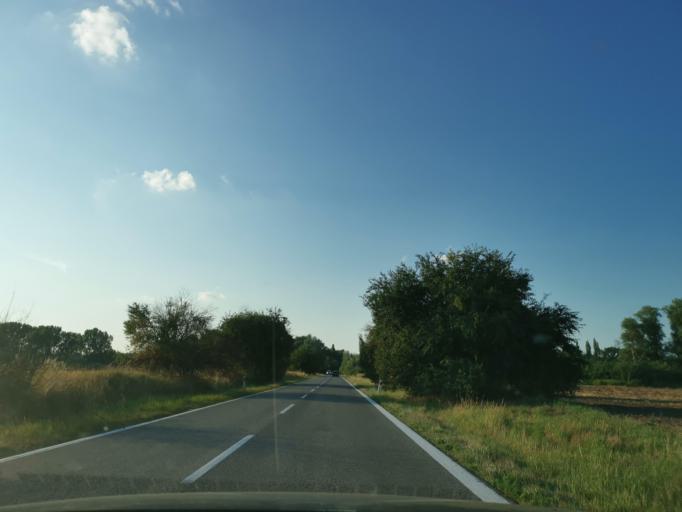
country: AT
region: Lower Austria
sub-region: Politischer Bezirk Ganserndorf
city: Drosing
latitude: 48.5311
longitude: 16.9838
